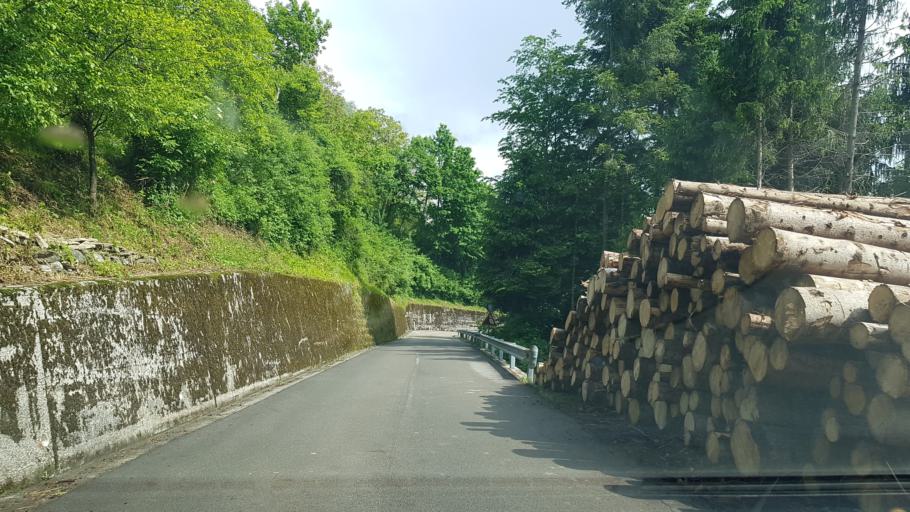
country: IT
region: Friuli Venezia Giulia
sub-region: Provincia di Udine
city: Arta Terme
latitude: 46.4698
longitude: 13.0062
